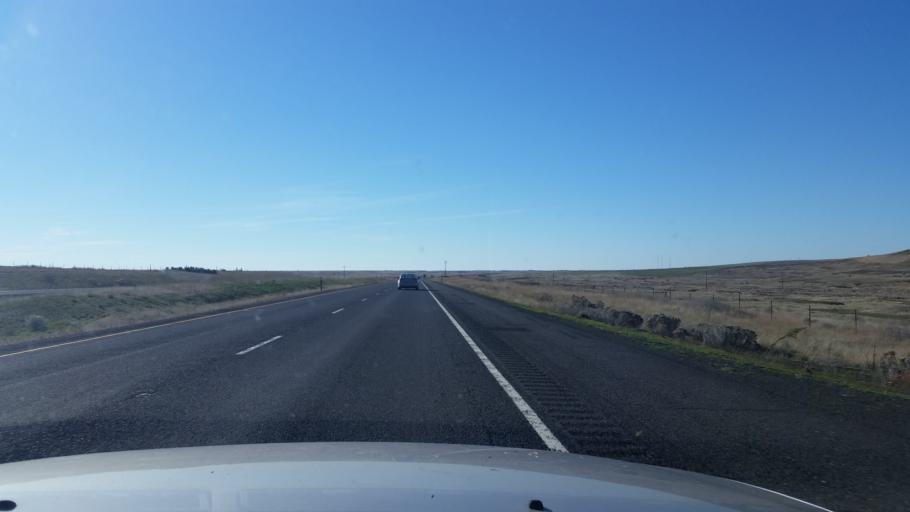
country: US
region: Washington
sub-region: Spokane County
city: Medical Lake
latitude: 47.3474
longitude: -117.9020
